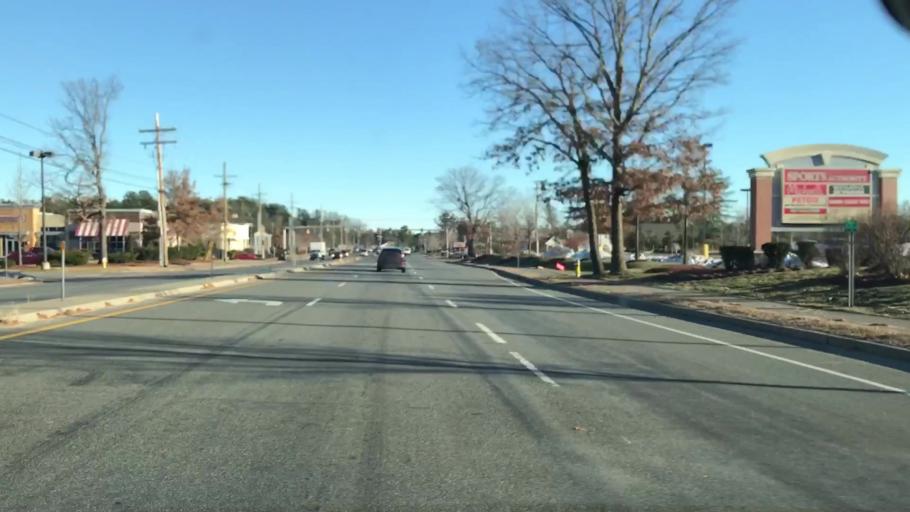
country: US
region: New Hampshire
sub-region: Hillsborough County
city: Hollis
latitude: 42.8078
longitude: -71.5697
